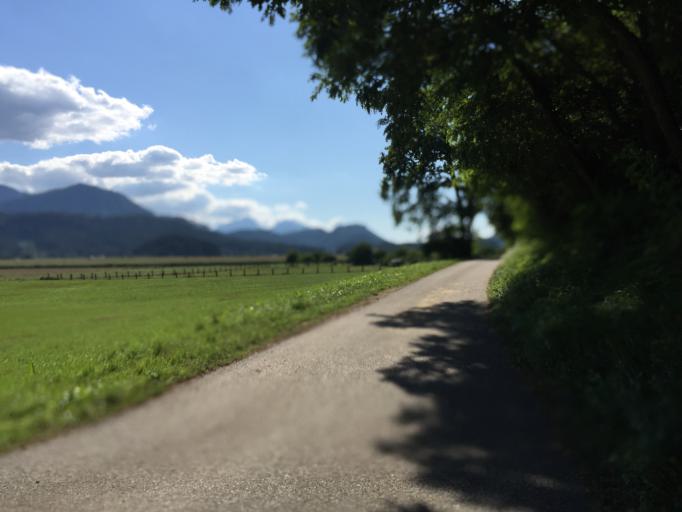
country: AT
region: Carinthia
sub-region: Politischer Bezirk Volkermarkt
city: Feistritz ob Bleiburg
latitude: 46.5592
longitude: 14.7435
